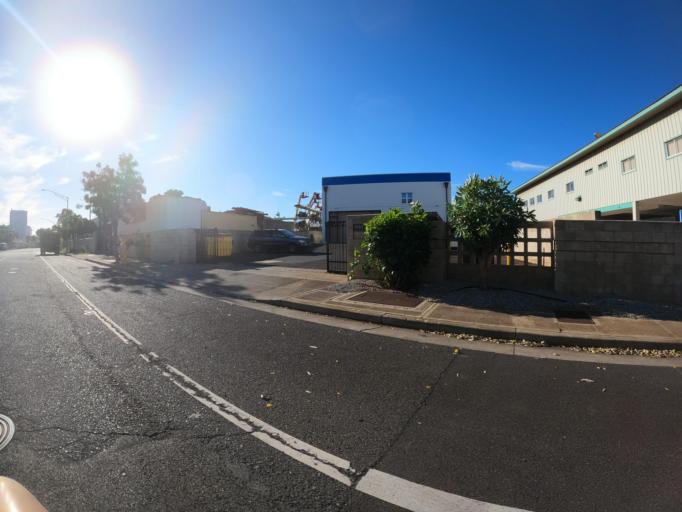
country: US
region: Hawaii
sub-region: Honolulu County
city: Honolulu
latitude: 21.3049
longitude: -157.8729
